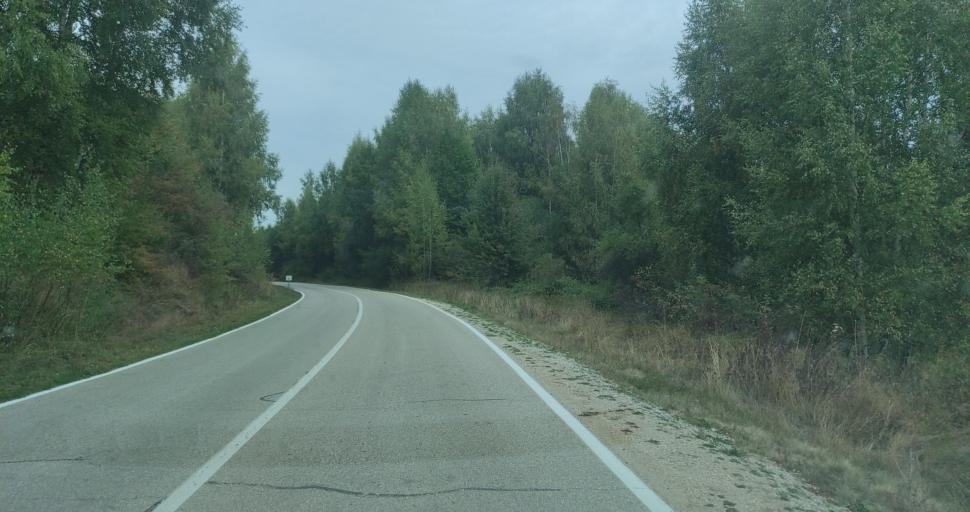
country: RS
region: Central Serbia
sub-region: Jablanicki Okrug
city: Crna Trava
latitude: 42.7127
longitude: 22.3283
